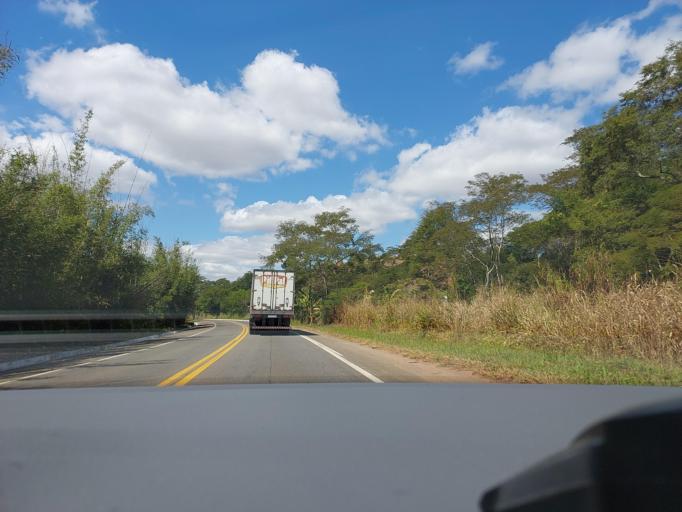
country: BR
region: Minas Gerais
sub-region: Muriae
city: Muriae
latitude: -21.1226
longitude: -42.2092
